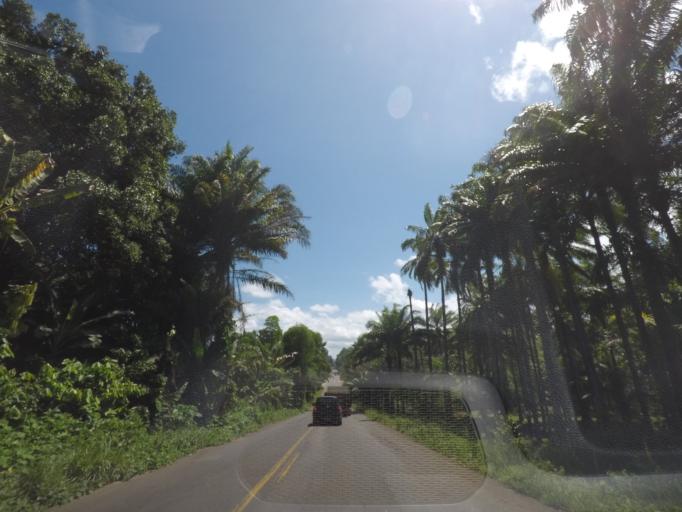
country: BR
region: Bahia
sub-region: Valenca
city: Valenca
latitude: -13.4480
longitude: -39.0850
